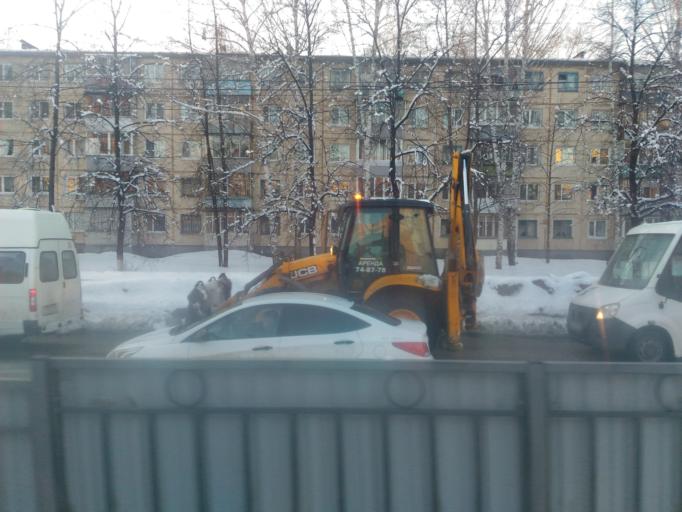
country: RU
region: Ulyanovsk
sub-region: Ulyanovskiy Rayon
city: Ulyanovsk
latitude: 54.2826
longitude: 48.2986
